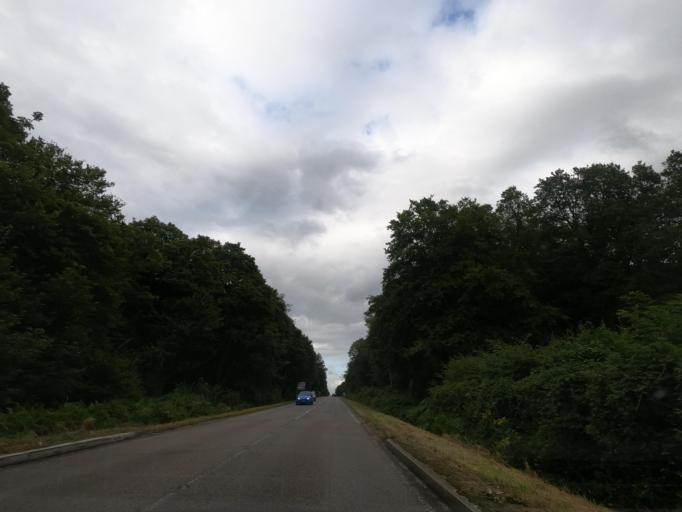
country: FR
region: Haute-Normandie
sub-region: Departement de l'Eure
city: Bourgtheroulde-Infreville
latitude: 49.3211
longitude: 0.9022
